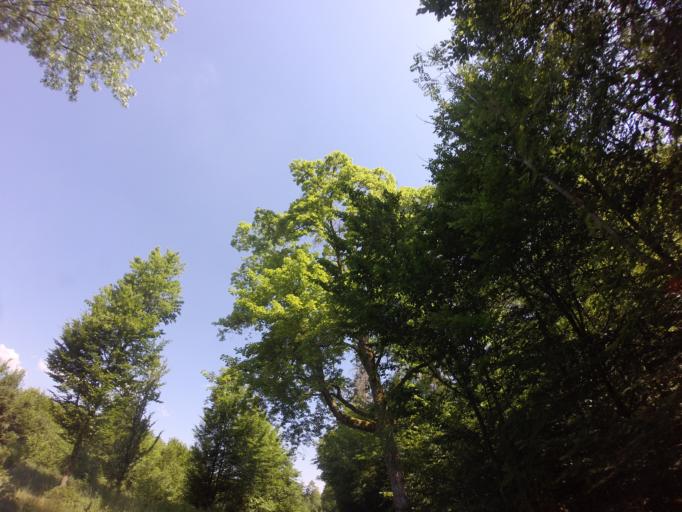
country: PL
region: West Pomeranian Voivodeship
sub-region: Powiat choszczenski
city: Drawno
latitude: 53.1685
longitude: 15.7914
